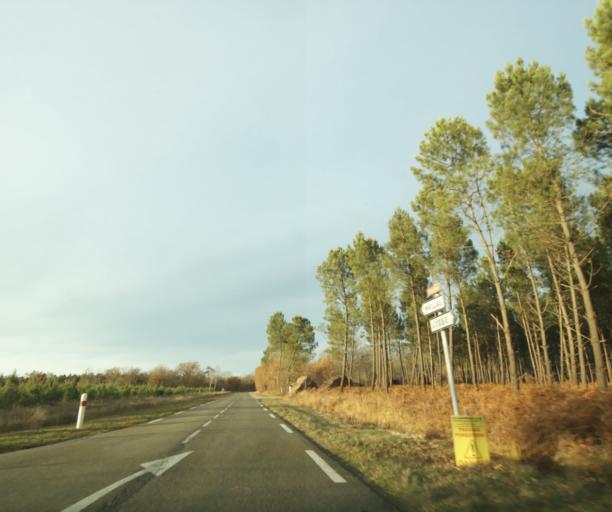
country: FR
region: Aquitaine
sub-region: Departement de la Gironde
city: Grignols
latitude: 44.1896
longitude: -0.1523
